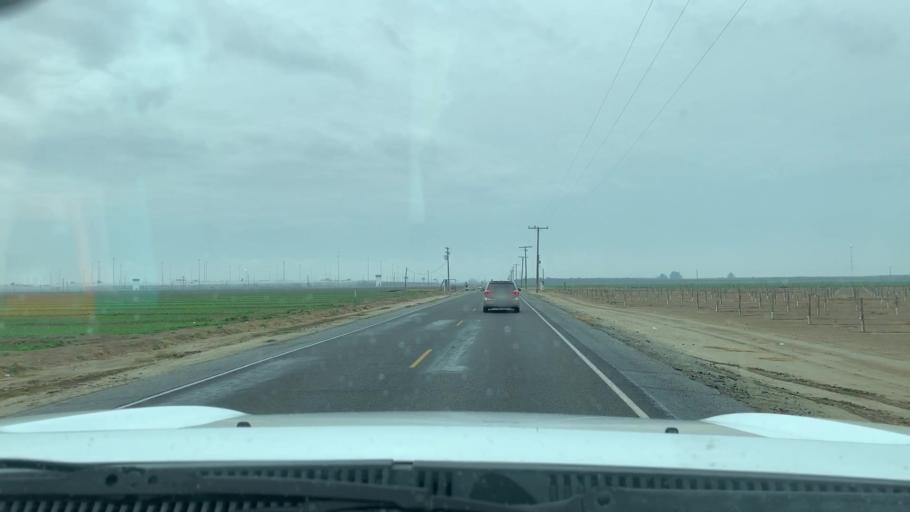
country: US
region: California
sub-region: Kern County
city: Delano
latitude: 35.7612
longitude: -119.3364
